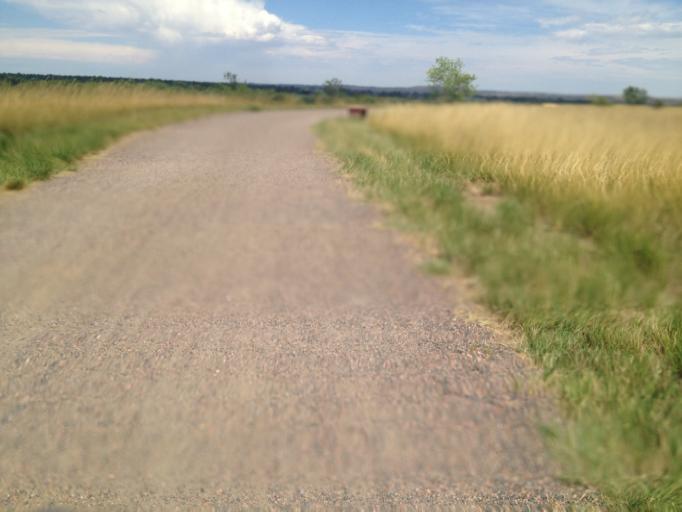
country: US
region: Colorado
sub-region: Boulder County
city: Louisville
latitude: 39.9751
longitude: -105.1130
